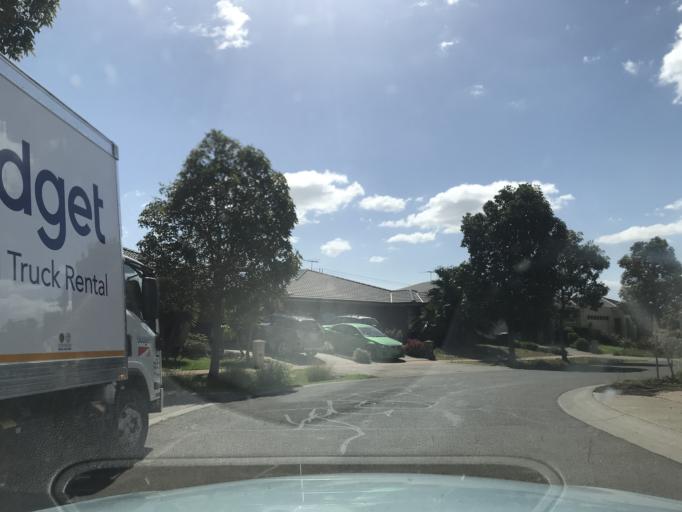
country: AU
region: Victoria
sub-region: Wyndham
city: Williams Landing
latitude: -37.8542
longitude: 144.7359
